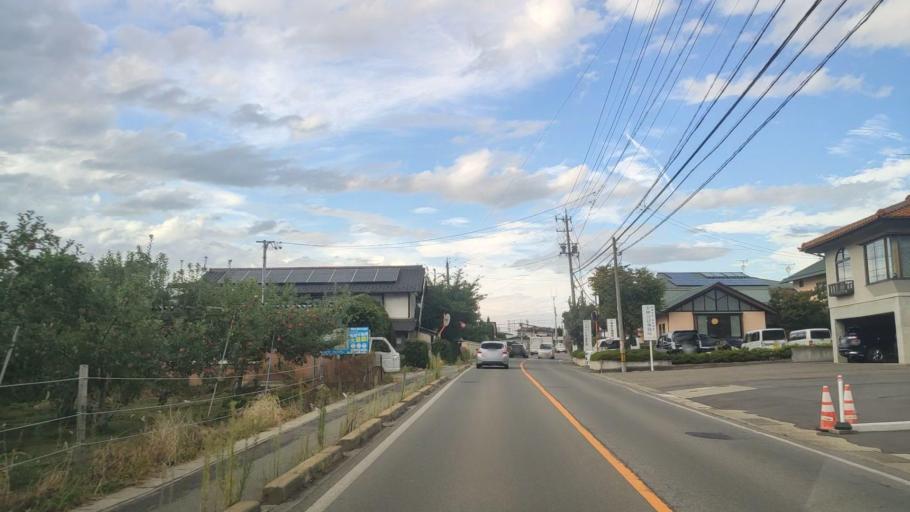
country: JP
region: Nagano
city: Suzaka
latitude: 36.6751
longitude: 138.3168
